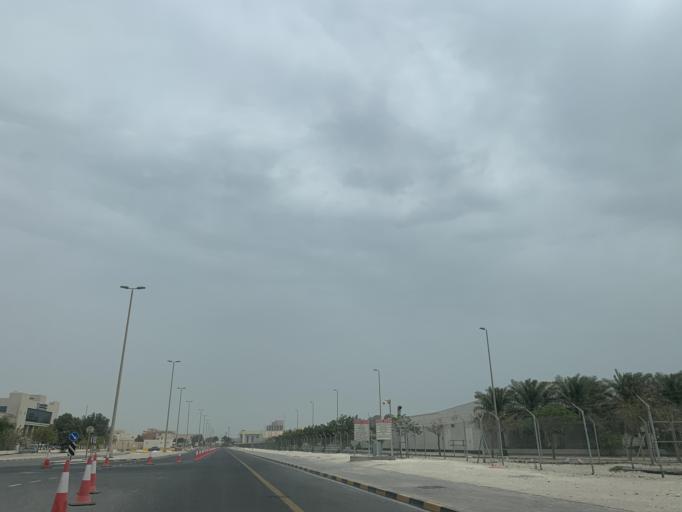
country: BH
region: Muharraq
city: Al Hadd
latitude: 26.2158
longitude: 50.6675
